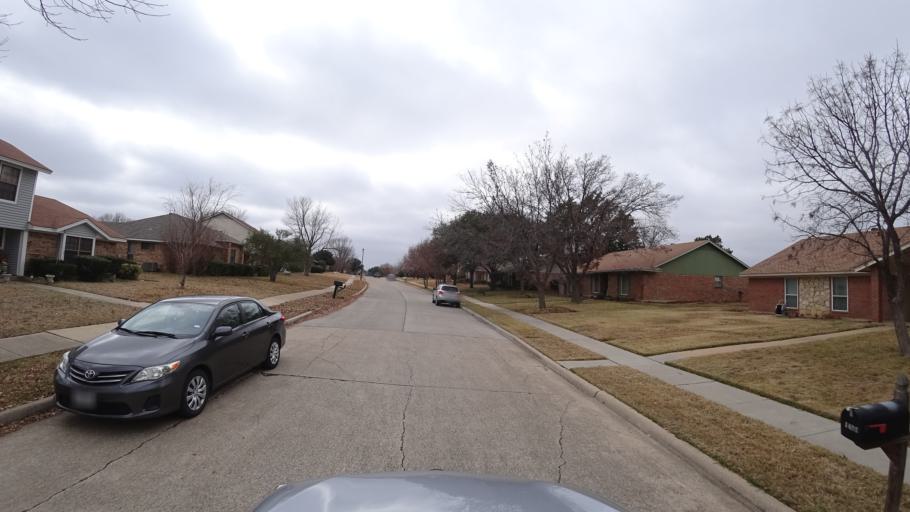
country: US
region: Texas
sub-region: Denton County
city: Lewisville
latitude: 33.0472
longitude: -97.0373
